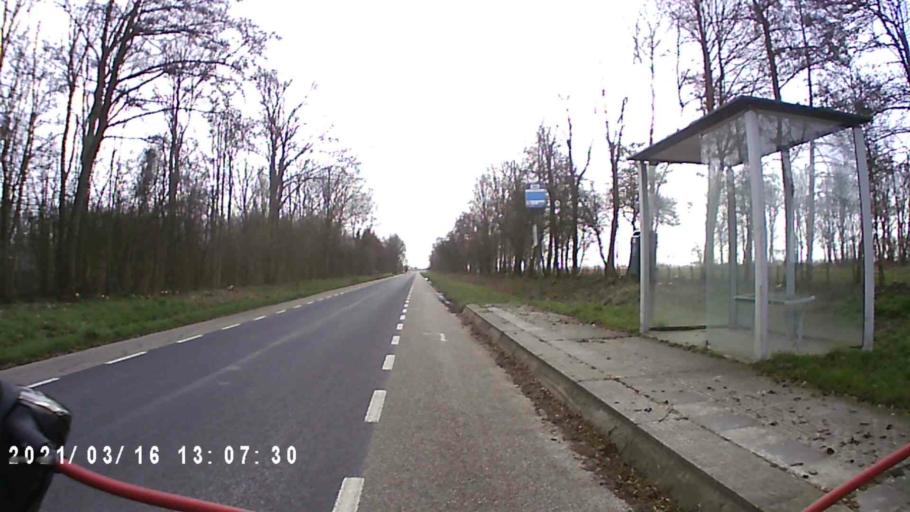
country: NL
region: Friesland
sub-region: Gemeente Het Bildt
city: Minnertsga
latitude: 53.2508
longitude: 5.6197
